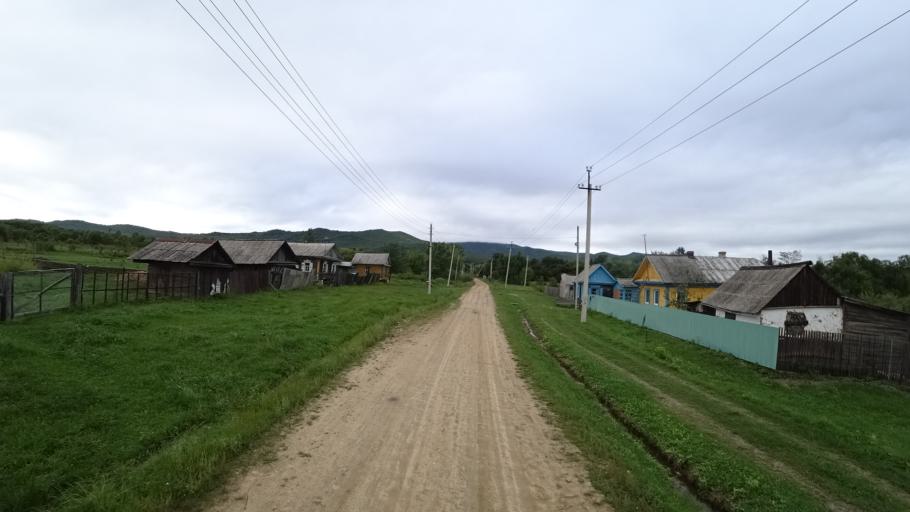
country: RU
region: Primorskiy
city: Rettikhovka
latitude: 44.1400
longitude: 132.6418
